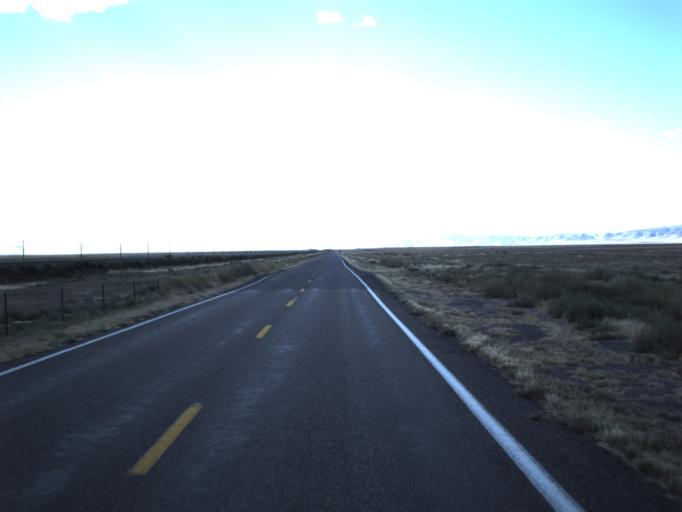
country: US
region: Utah
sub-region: Millard County
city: Delta
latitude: 39.0073
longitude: -112.7847
